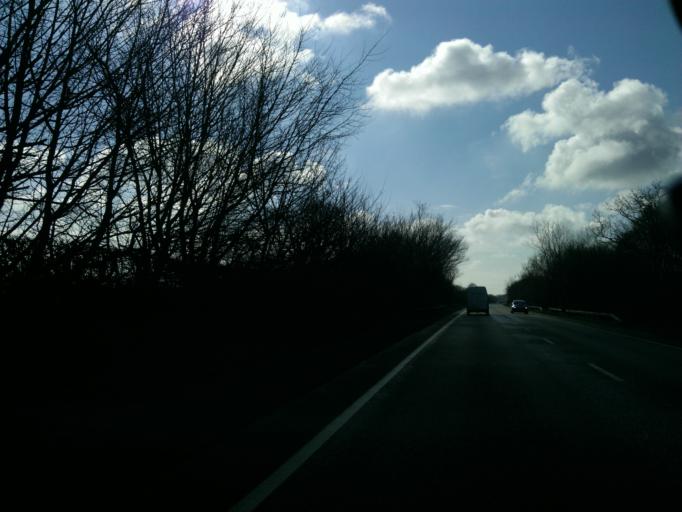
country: GB
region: England
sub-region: Essex
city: Little Clacton
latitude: 51.8304
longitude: 1.1296
